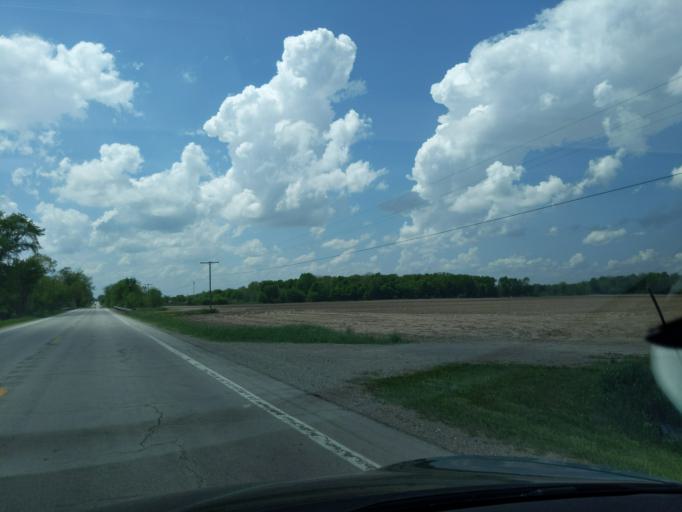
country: US
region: Michigan
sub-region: Ingham County
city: Stockbridge
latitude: 42.5517
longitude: -84.1994
